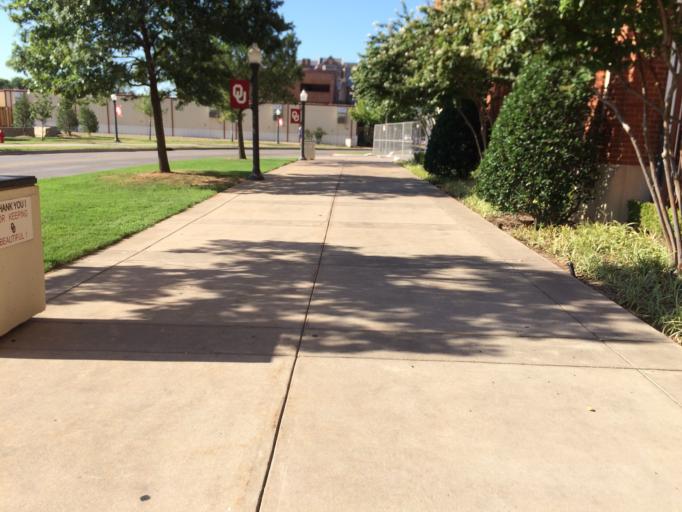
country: US
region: Oklahoma
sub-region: Cleveland County
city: Norman
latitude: 35.2056
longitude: -97.4412
